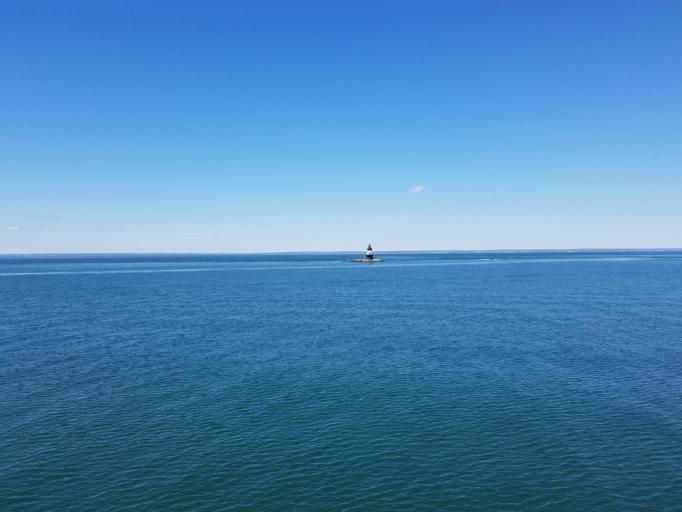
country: US
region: New York
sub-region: Suffolk County
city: Shelter Island
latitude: 41.1553
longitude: -72.2236
